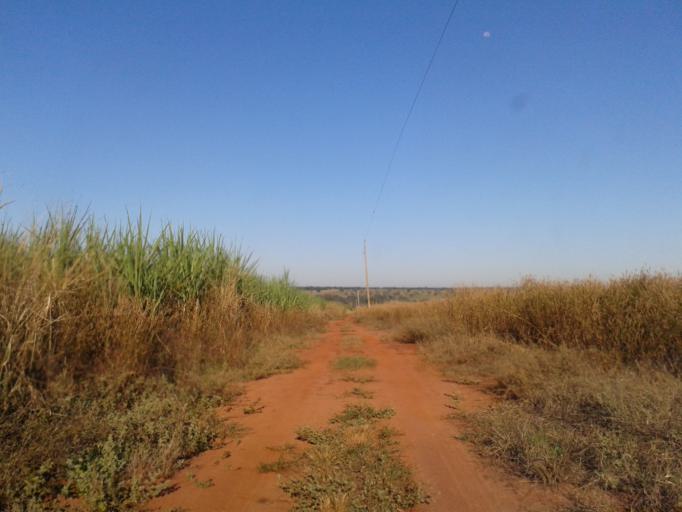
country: BR
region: Minas Gerais
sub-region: Santa Vitoria
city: Santa Vitoria
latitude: -19.0213
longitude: -50.3621
